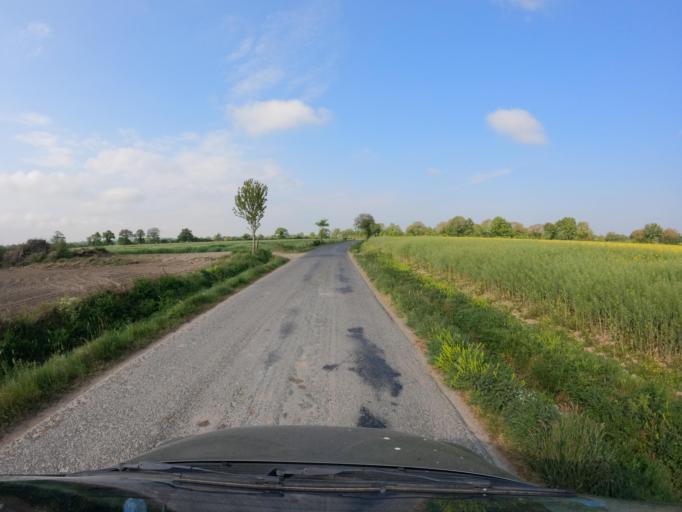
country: FR
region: Pays de la Loire
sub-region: Departement de Maine-et-Loire
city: Roussay
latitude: 47.0701
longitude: -1.0786
